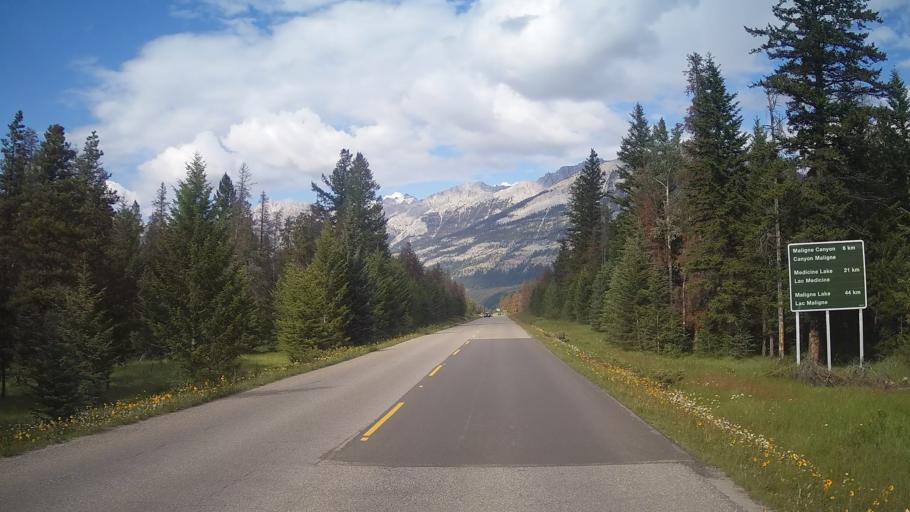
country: CA
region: Alberta
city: Jasper Park Lodge
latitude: 52.9111
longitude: -118.0532
